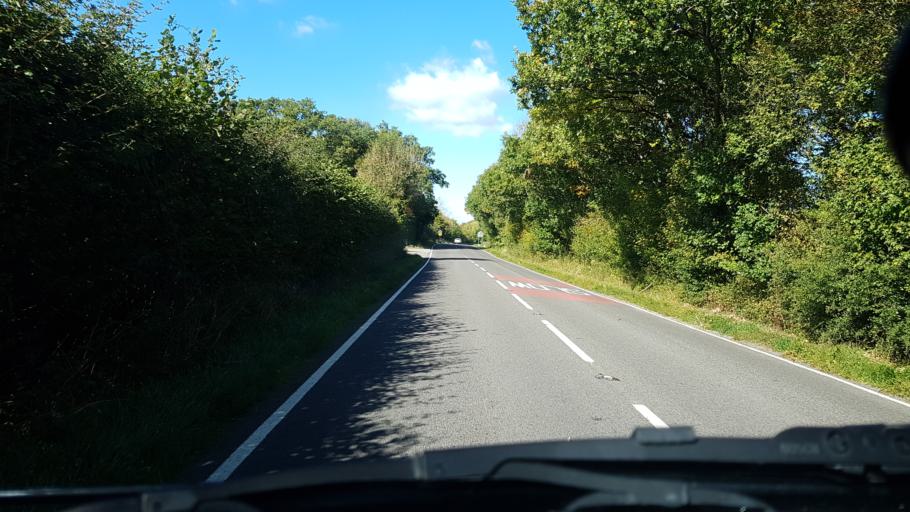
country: GB
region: England
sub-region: West Sussex
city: Billingshurst
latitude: 51.0062
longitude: -0.4286
